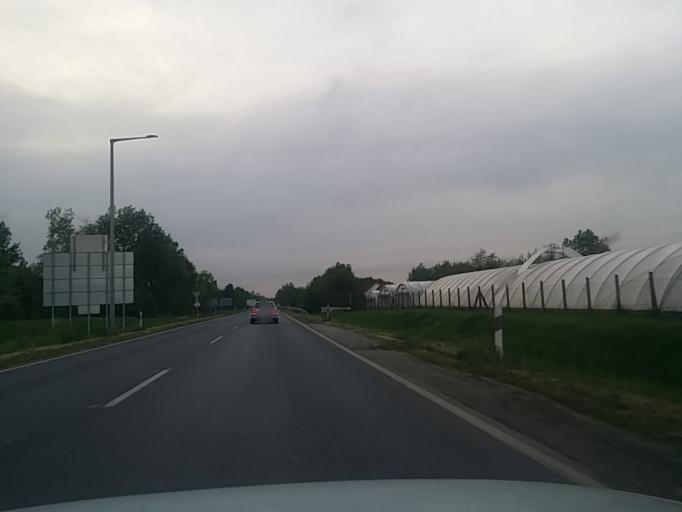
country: HU
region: Bekes
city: Gyula
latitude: 46.6340
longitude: 21.2569
